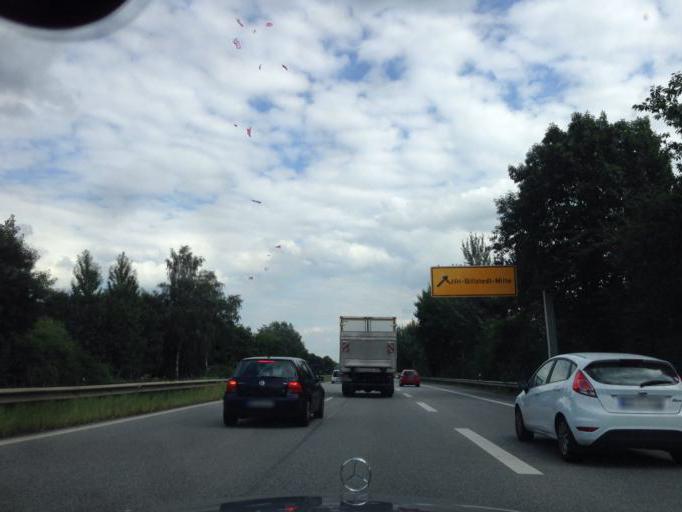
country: DE
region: Hamburg
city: Wandsbek
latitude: 53.5413
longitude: 10.0926
